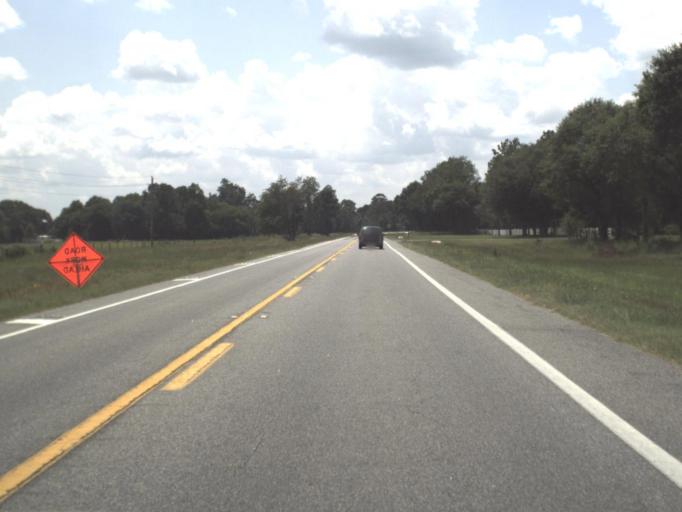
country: US
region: Florida
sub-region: Hamilton County
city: Jasper
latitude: 30.5239
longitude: -83.0179
